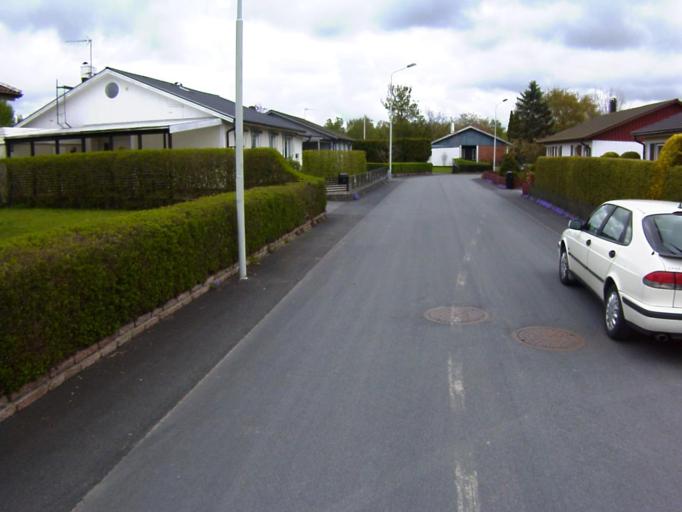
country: SE
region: Skane
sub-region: Kristianstads Kommun
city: Kristianstad
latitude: 56.0495
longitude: 14.1752
